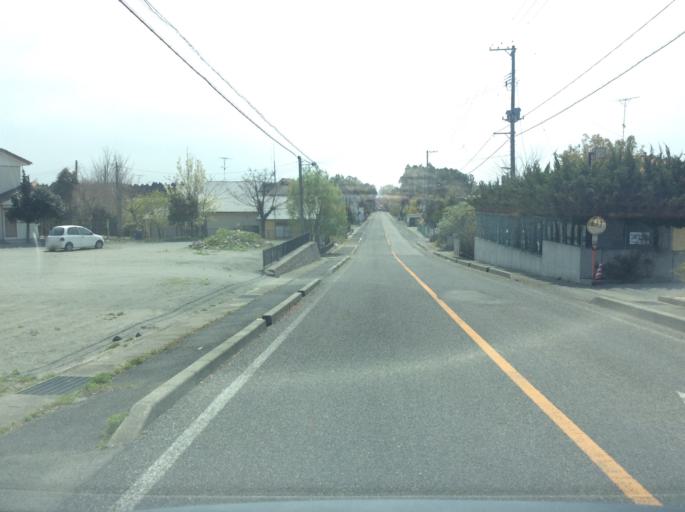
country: JP
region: Fukushima
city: Namie
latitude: 37.3579
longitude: 140.9961
